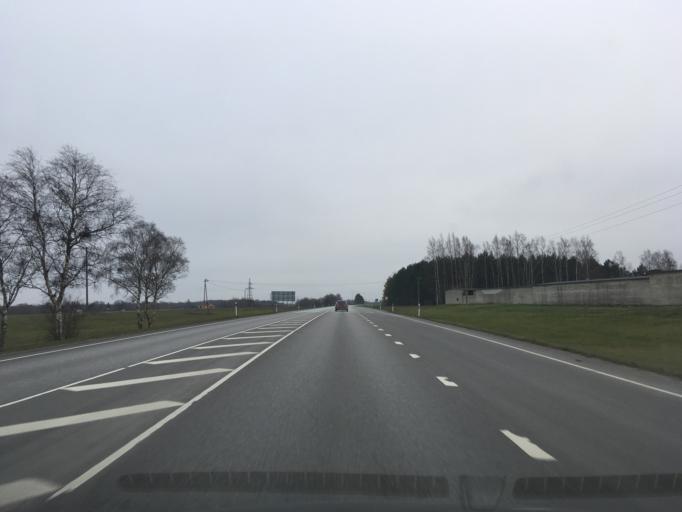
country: EE
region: Ida-Virumaa
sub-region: Kohtla-Jaerve linn
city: Kohtla-Jarve
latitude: 59.4099
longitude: 27.3121
